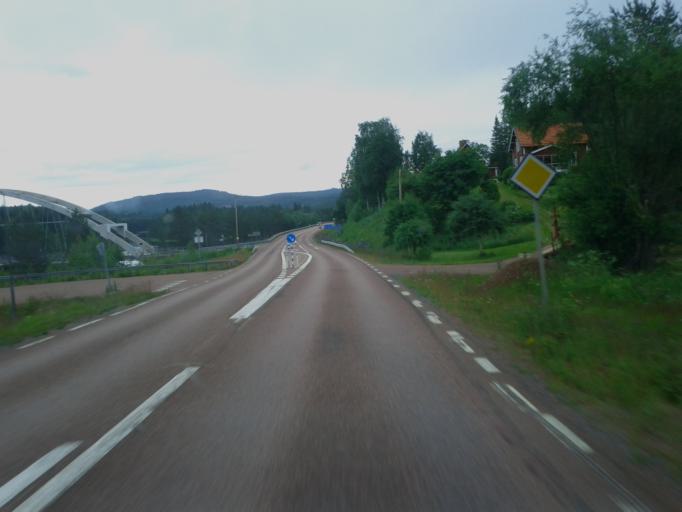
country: SE
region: Dalarna
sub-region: Alvdalens Kommun
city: AElvdalen
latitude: 61.2802
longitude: 13.7645
